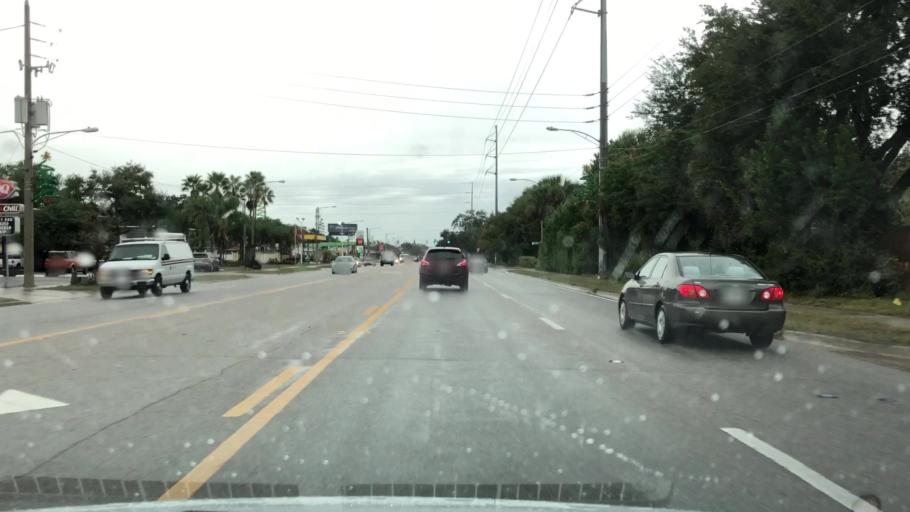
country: US
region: Florida
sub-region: Orange County
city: Conway
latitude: 28.5243
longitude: -81.3368
